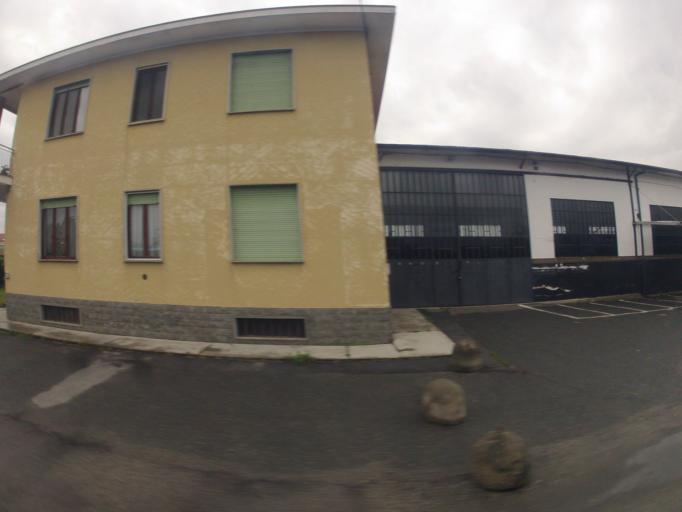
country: IT
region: Piedmont
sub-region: Provincia di Torino
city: Carignano
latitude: 44.8950
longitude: 7.6697
